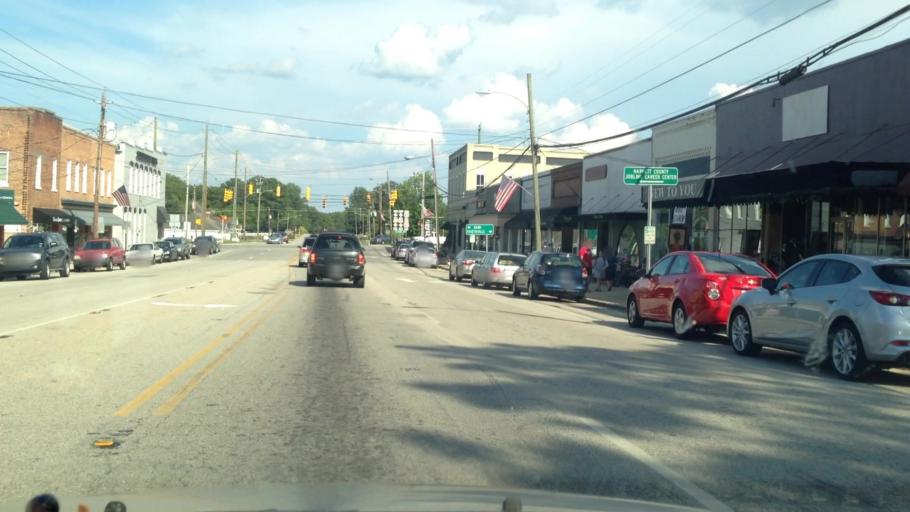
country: US
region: North Carolina
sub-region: Harnett County
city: Lillington
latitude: 35.3990
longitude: -78.8176
